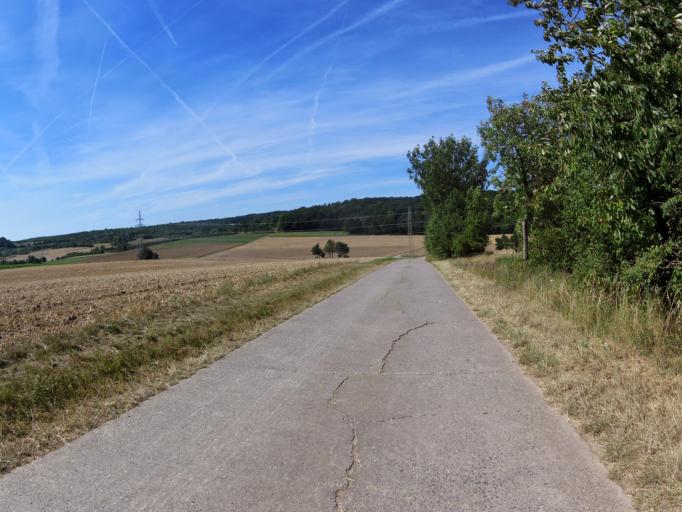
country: DE
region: Bavaria
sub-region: Regierungsbezirk Unterfranken
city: Hettstadt
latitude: 49.8120
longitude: 9.8114
